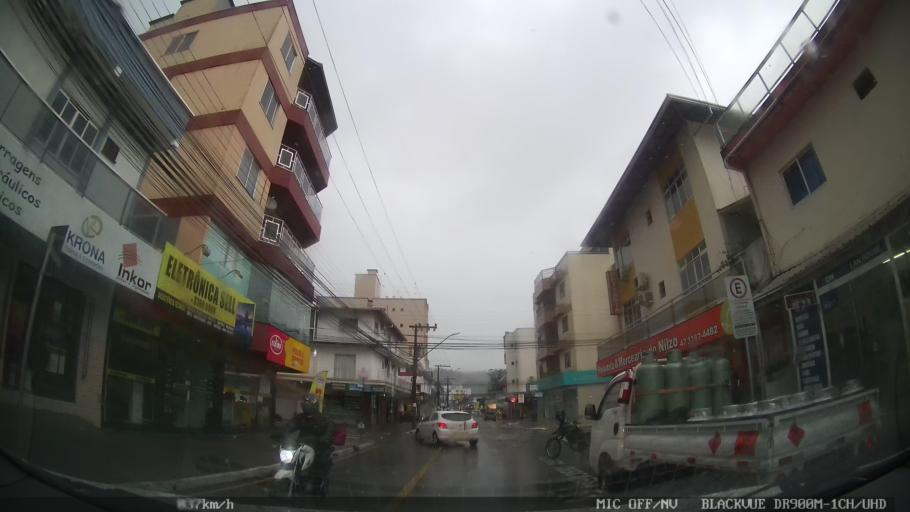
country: BR
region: Santa Catarina
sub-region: Balneario Camboriu
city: Balneario Camboriu
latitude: -26.9757
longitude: -48.6461
